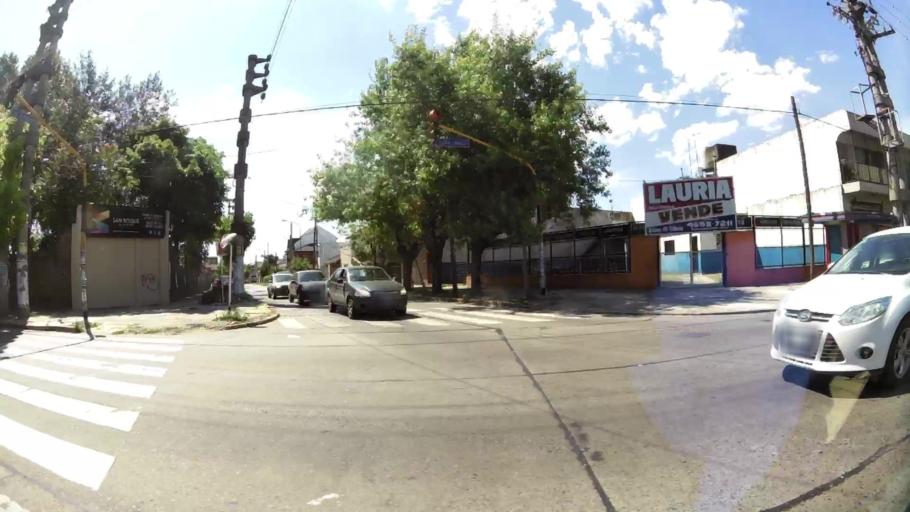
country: AR
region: Buenos Aires
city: San Justo
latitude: -34.6679
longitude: -58.5536
